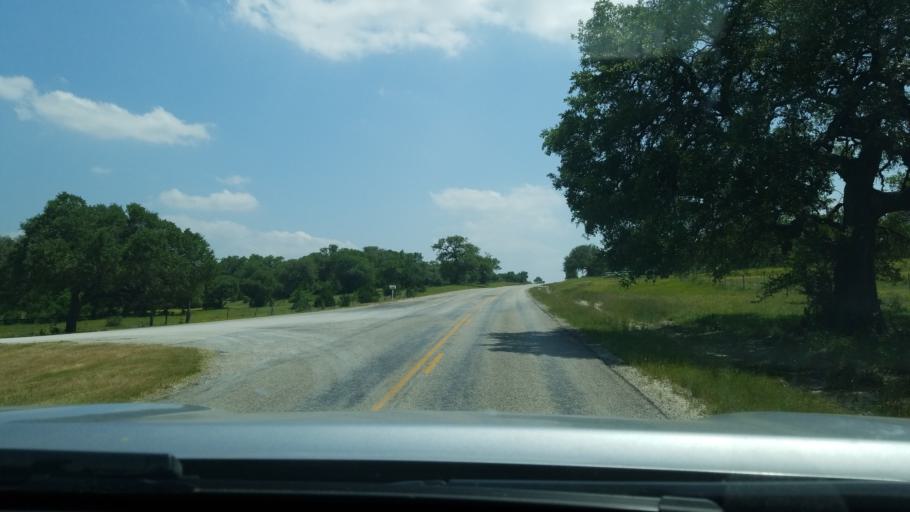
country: US
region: Texas
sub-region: Bexar County
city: Fair Oaks Ranch
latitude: 29.9417
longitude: -98.5659
